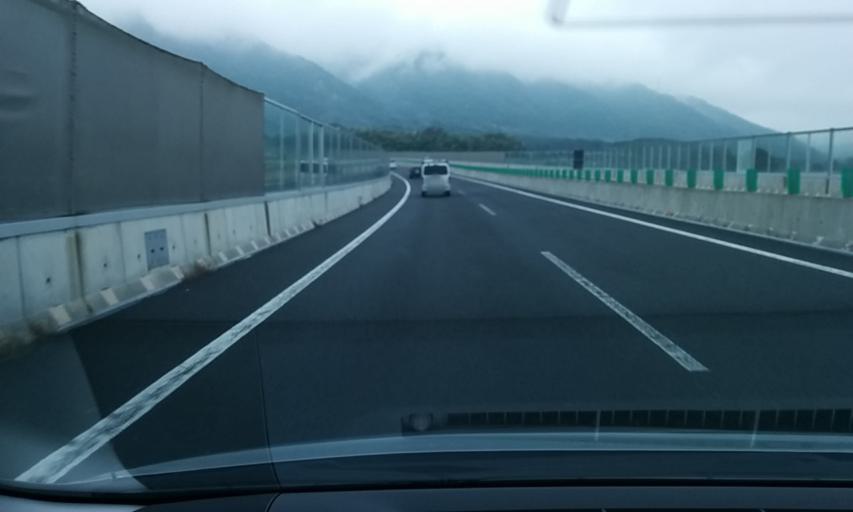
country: JP
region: Kyoto
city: Muko
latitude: 34.9523
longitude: 135.6604
